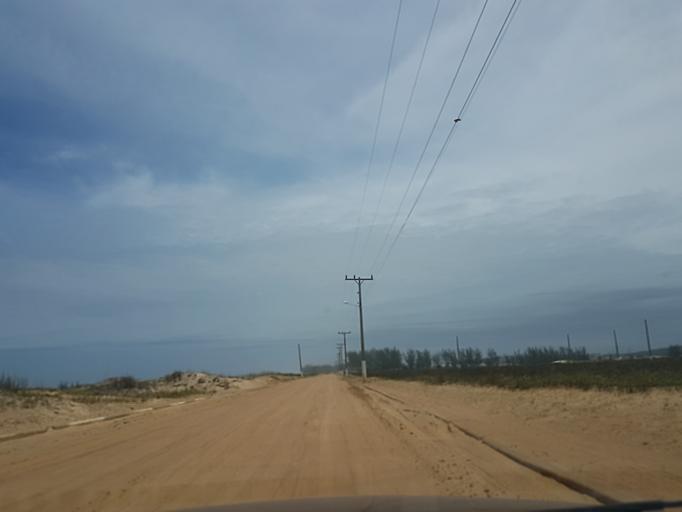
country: BR
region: Santa Catarina
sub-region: Jaguaruna
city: Jaguaruna
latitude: -28.6665
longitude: -48.9667
